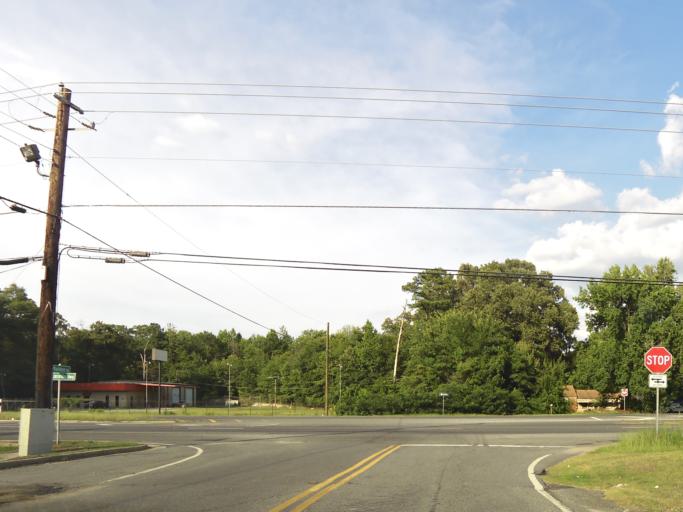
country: US
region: Georgia
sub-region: Houston County
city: Centerville
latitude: 32.7138
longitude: -83.6484
